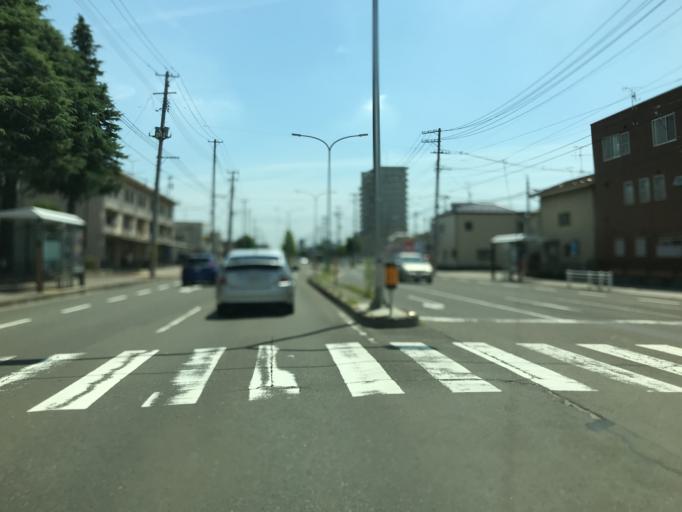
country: JP
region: Miyagi
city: Sendai-shi
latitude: 38.2730
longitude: 140.8923
